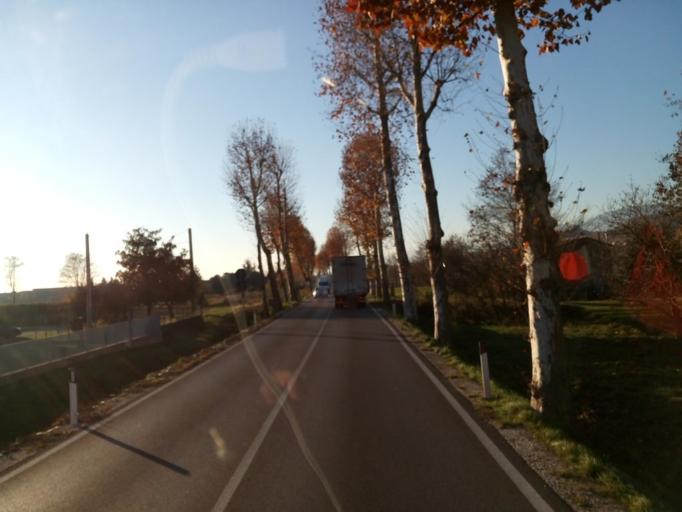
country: IT
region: Veneto
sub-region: Provincia di Treviso
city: Maser
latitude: 45.7948
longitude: 11.9561
